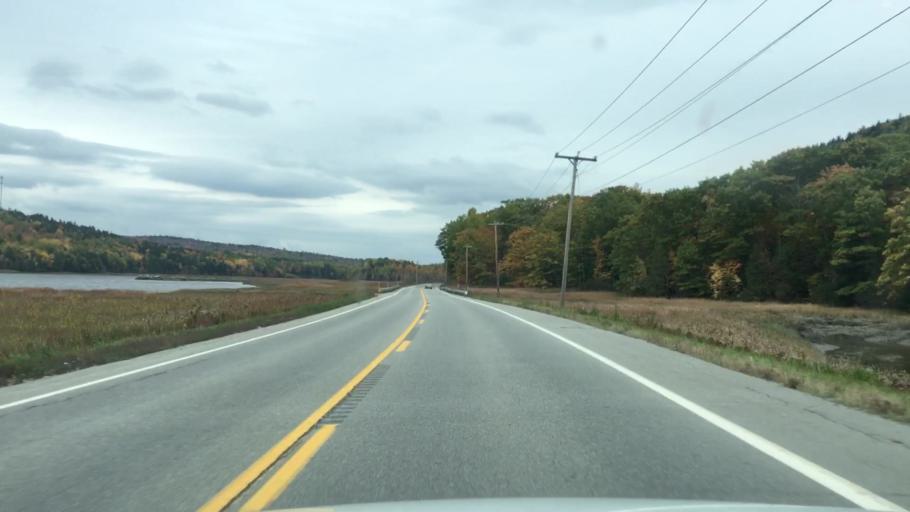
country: US
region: Maine
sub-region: Waldo County
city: Frankfort
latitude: 44.5890
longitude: -68.8654
